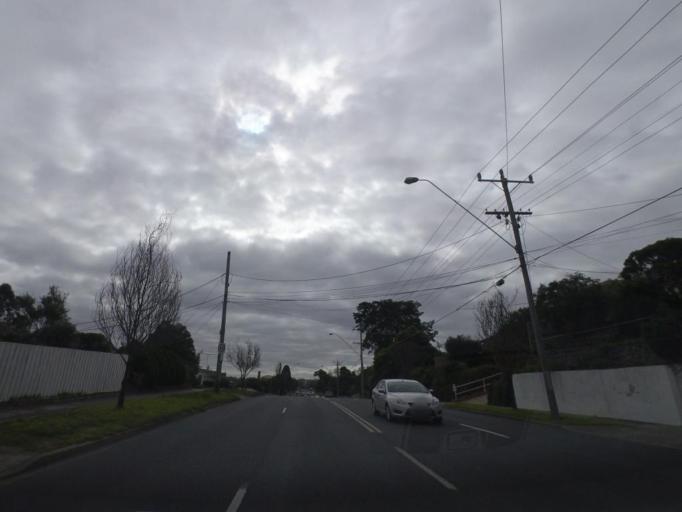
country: AU
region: Victoria
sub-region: Whitehorse
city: Box Hill North
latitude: -37.8069
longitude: 145.1168
